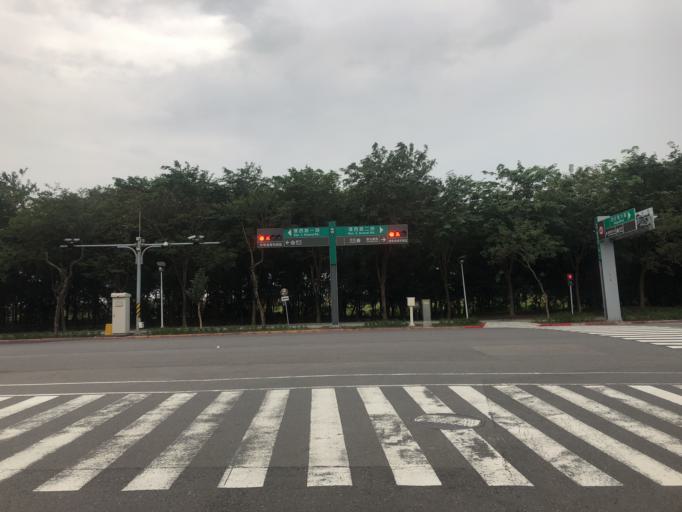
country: TW
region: Taiwan
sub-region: Tainan
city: Tainan
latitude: 23.1014
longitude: 120.2756
